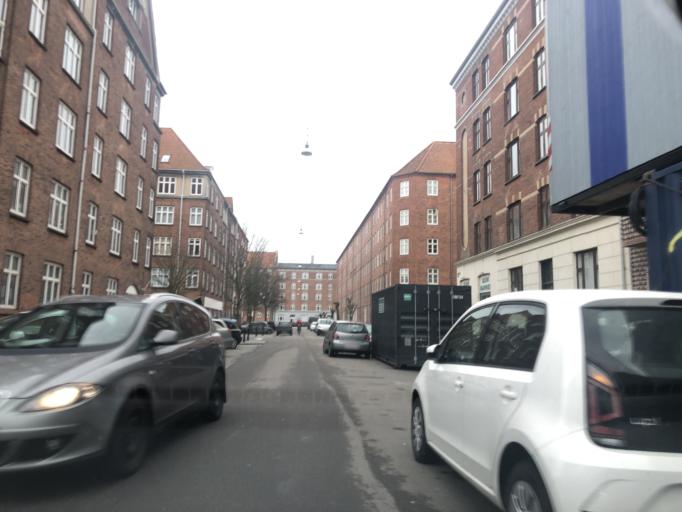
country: DK
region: Capital Region
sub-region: Kobenhavn
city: Christianshavn
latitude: 55.6562
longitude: 12.6130
